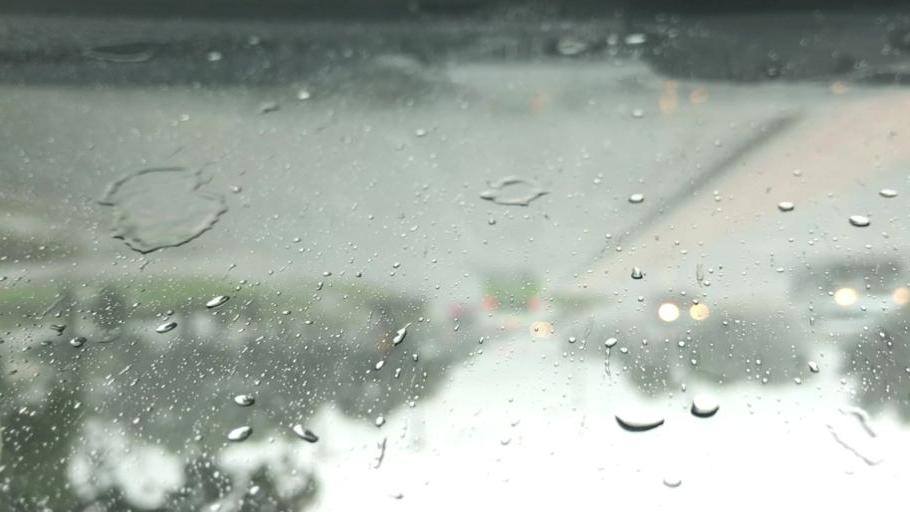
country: US
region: Texas
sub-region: Williamson County
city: Leander
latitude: 30.5438
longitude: -97.8639
